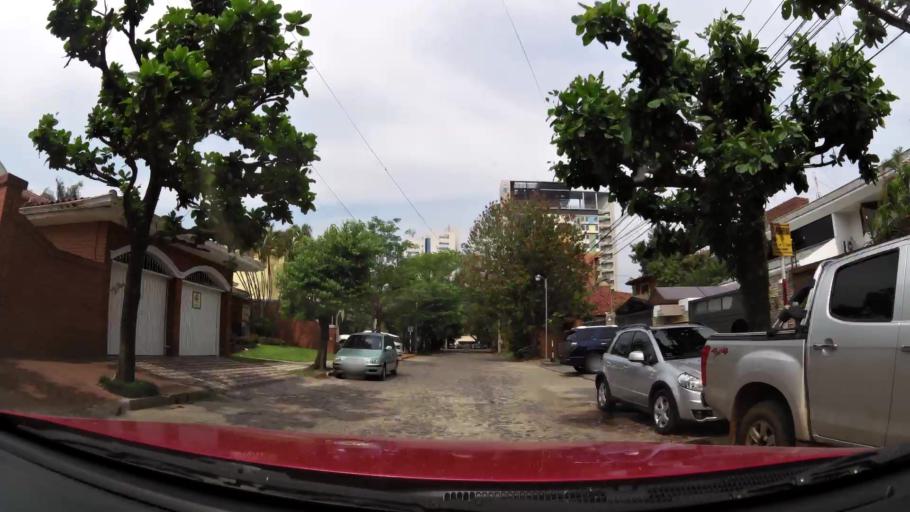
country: PY
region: Asuncion
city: Asuncion
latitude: -25.2844
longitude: -57.5704
